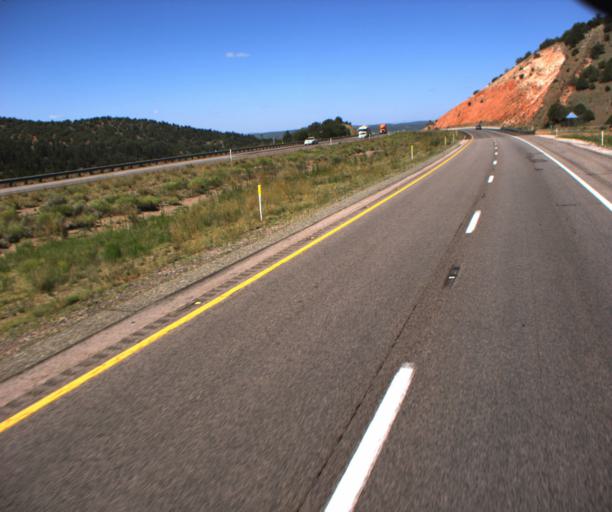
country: US
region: Arizona
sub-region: Mohave County
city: Peach Springs
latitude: 35.2877
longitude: -113.1139
